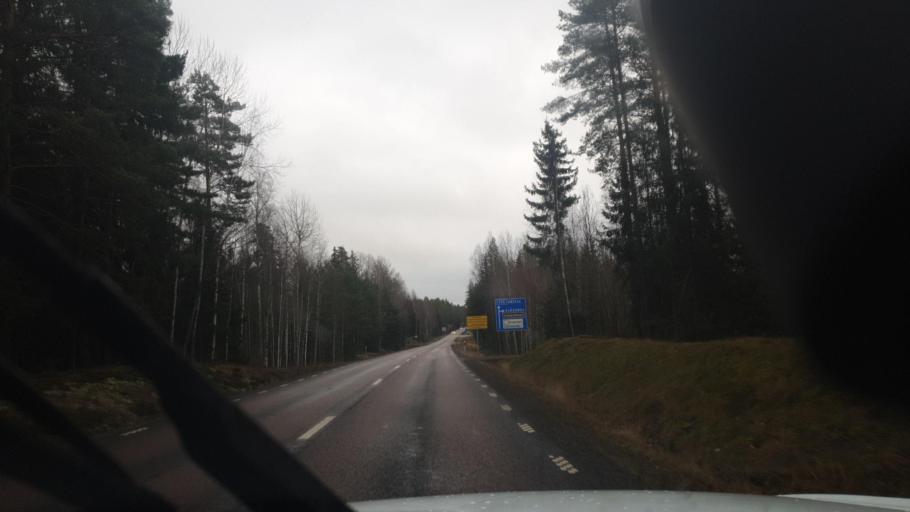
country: SE
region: Vaermland
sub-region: Arvika Kommun
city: Arvika
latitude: 59.5449
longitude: 12.7429
